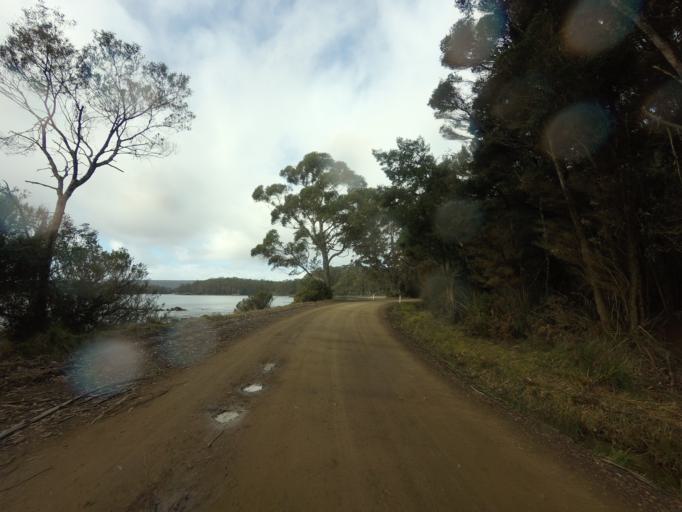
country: AU
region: Tasmania
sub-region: Huon Valley
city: Geeveston
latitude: -43.5465
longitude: 146.8893
